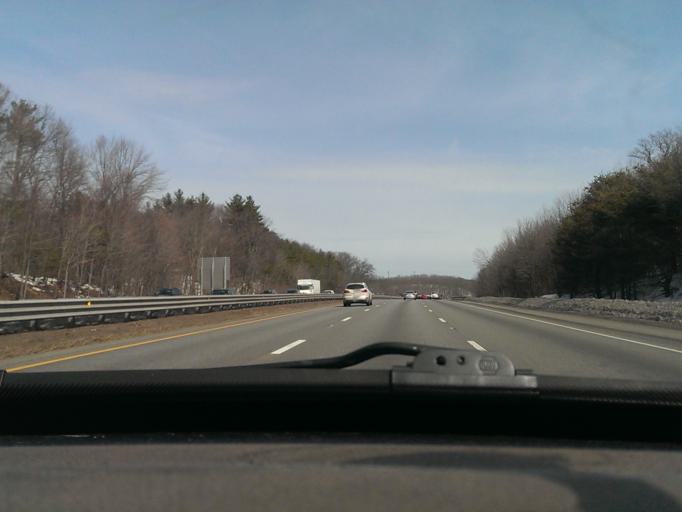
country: US
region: Massachusetts
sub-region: Worcester County
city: Charlton
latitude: 42.1721
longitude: -71.9287
